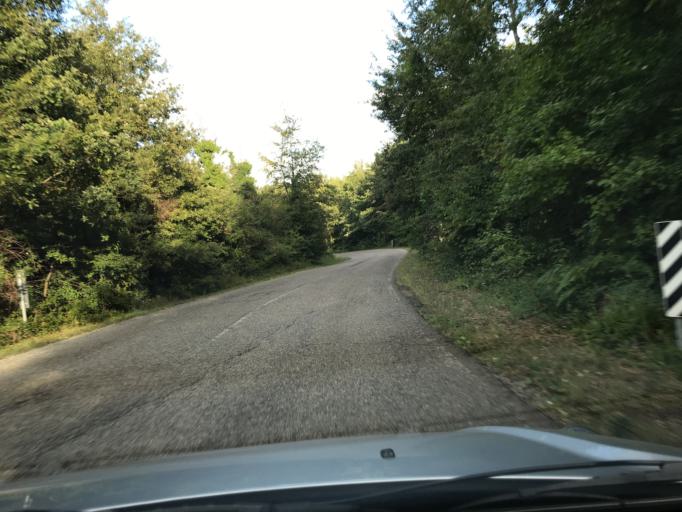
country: IT
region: Umbria
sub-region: Provincia di Terni
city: Guardea
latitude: 42.6473
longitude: 12.3530
